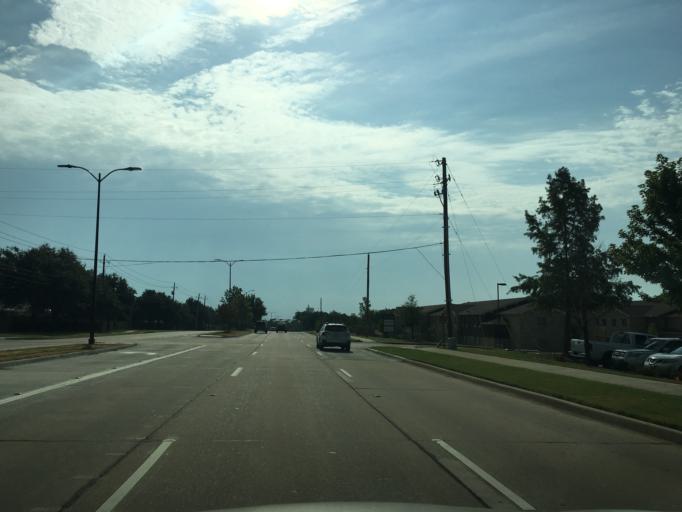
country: US
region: Texas
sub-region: Collin County
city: Fairview
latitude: 33.1986
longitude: -96.6907
